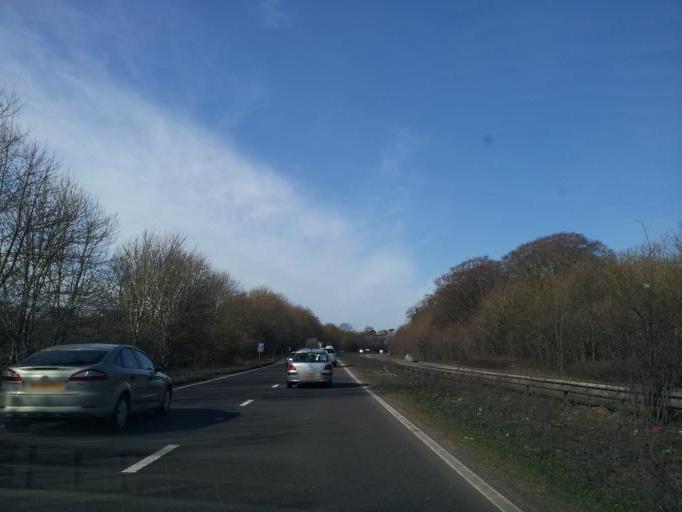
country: GB
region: England
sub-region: Lincolnshire
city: Grantham
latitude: 52.8245
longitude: -0.6288
